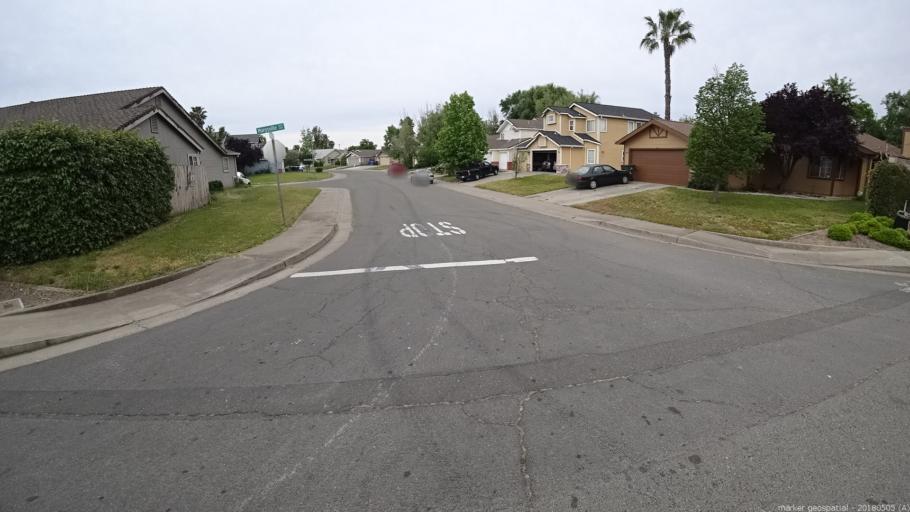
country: US
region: California
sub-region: Sacramento County
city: Rio Linda
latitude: 38.6577
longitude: -121.4434
